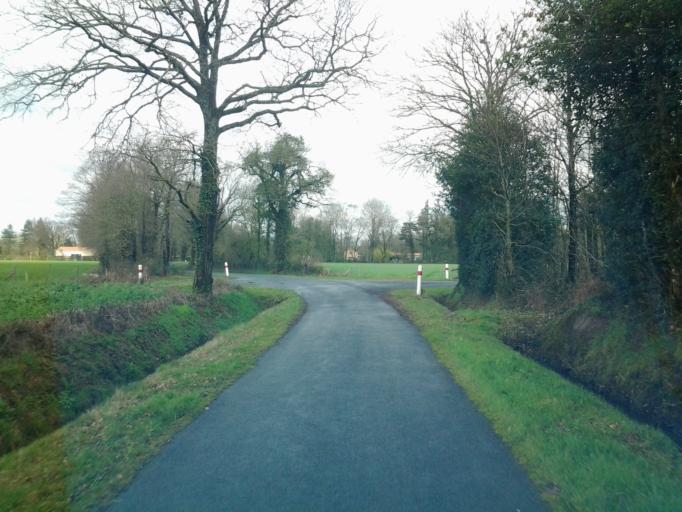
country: FR
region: Pays de la Loire
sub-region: Departement de la Vendee
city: La Chaize-le-Vicomte
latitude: 46.6619
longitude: -1.3411
